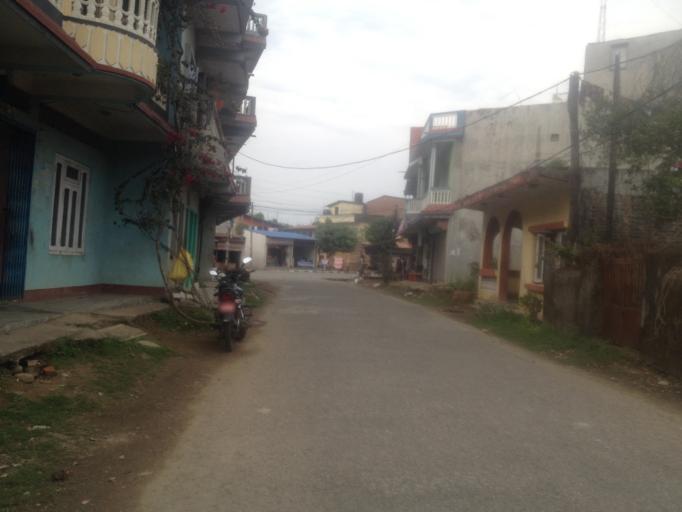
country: NP
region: Central Region
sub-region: Narayani Zone
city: Bharatpur
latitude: 27.6899
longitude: 84.4361
